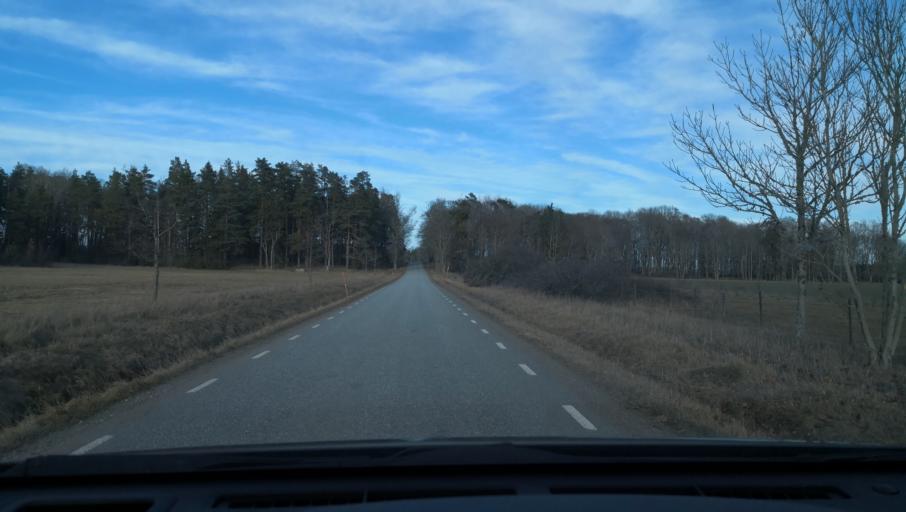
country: SE
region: Uppsala
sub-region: Enkopings Kommun
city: Grillby
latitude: 59.5460
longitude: 17.2096
